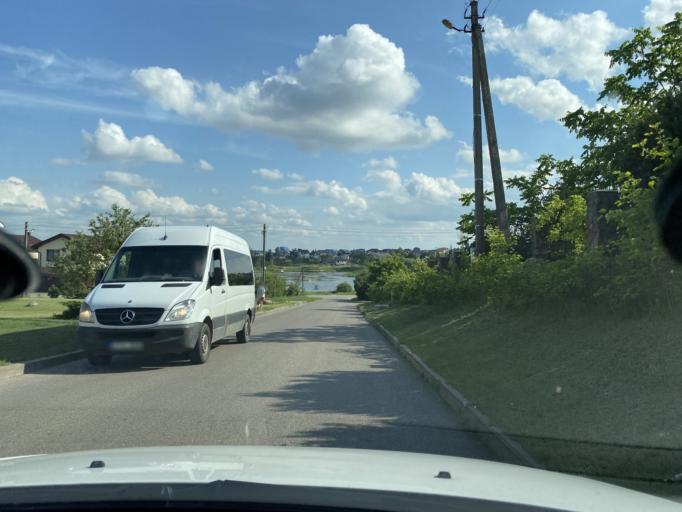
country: LT
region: Vilnius County
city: Pasilaiciai
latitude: 54.7370
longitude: 25.1982
